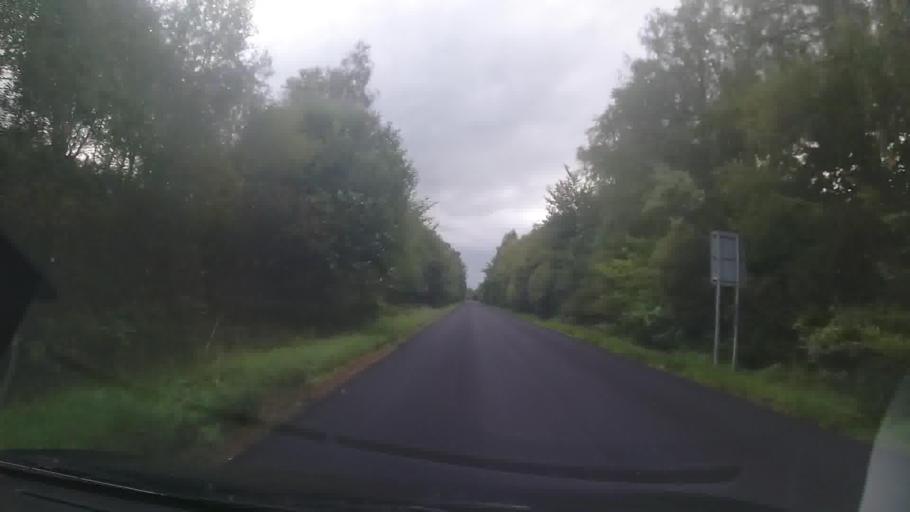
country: GB
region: Scotland
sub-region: Argyll and Bute
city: Garelochhead
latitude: 56.2384
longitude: -4.9601
